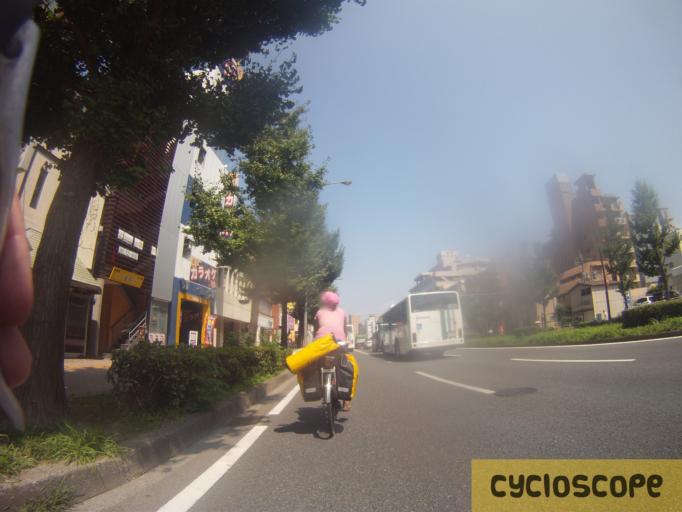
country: JP
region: Fukuoka
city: Fukuoka-shi
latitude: 33.5873
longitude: 130.3653
